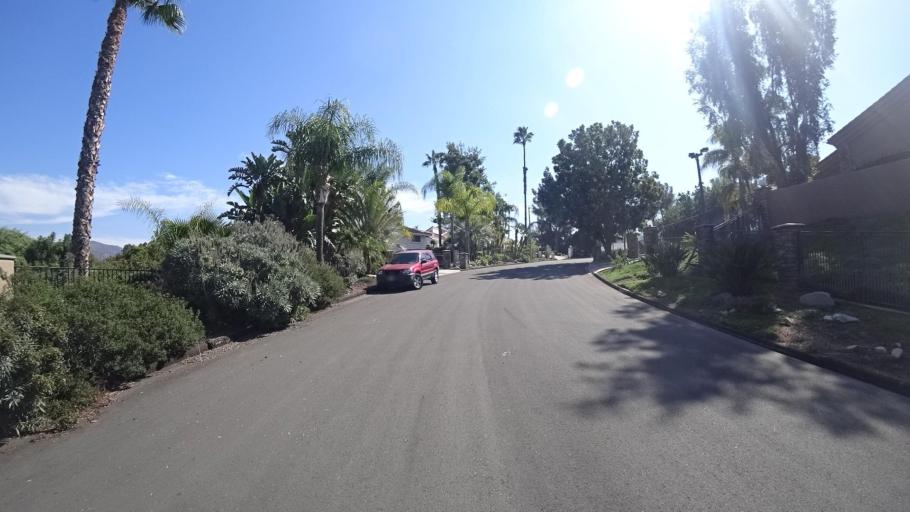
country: US
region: California
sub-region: San Diego County
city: Granite Hills
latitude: 32.7864
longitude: -116.9028
